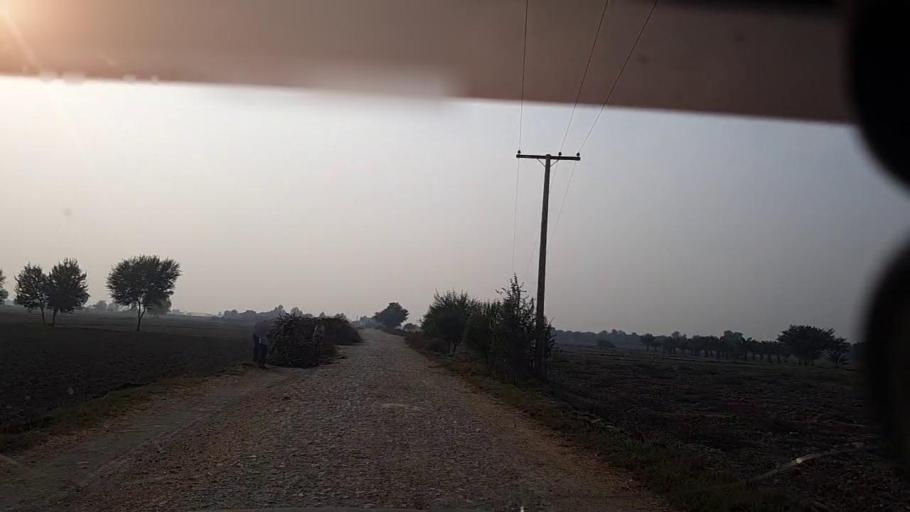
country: PK
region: Sindh
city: Kot Diji
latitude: 27.4367
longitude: 68.6223
